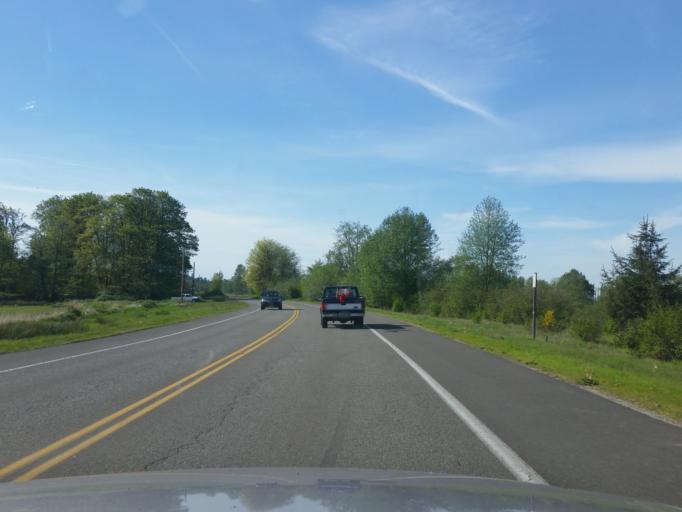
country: US
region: Washington
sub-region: Snohomish County
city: Everett
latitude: 47.9411
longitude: -122.1726
